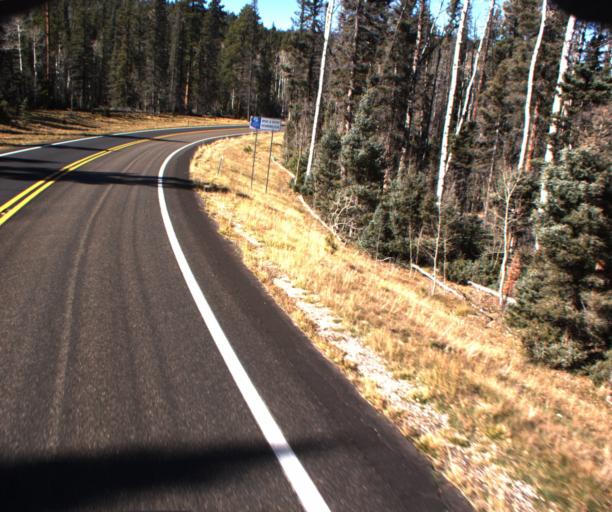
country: US
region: Arizona
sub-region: Coconino County
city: Grand Canyon
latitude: 36.4497
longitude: -112.1339
